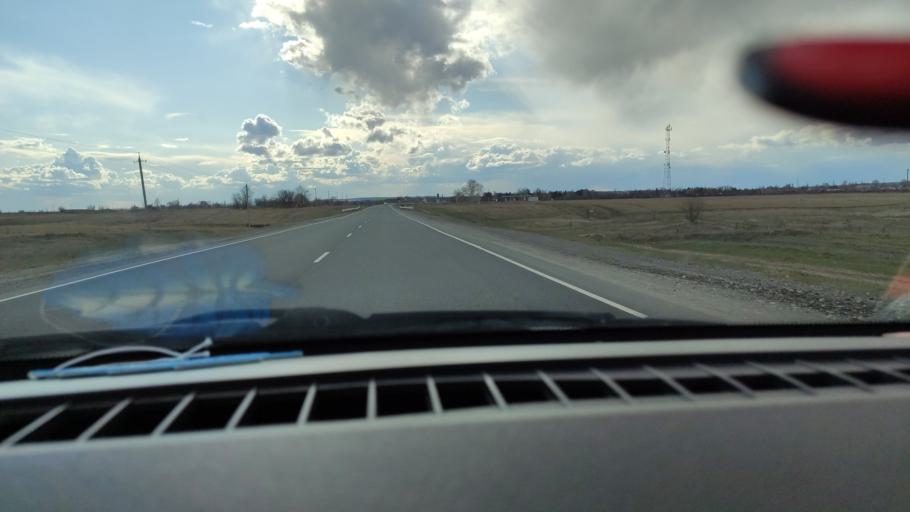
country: RU
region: Saratov
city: Sennoy
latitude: 52.1501
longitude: 46.9807
